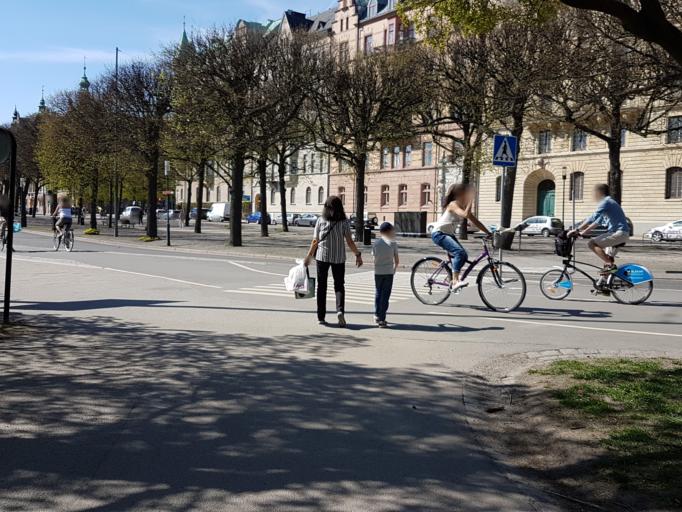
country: SE
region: Stockholm
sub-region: Stockholms Kommun
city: OEstermalm
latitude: 59.3317
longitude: 18.0958
